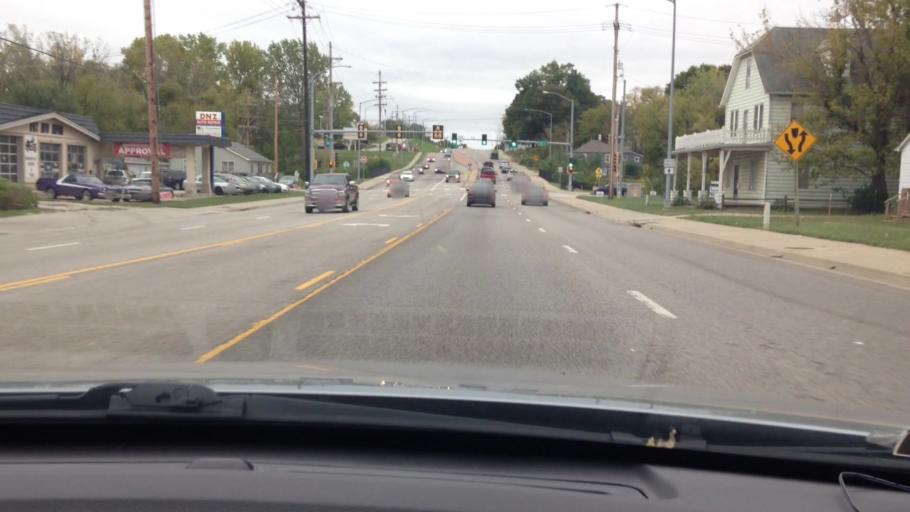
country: US
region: Kansas
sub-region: Leavenworth County
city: Lansing
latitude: 39.2527
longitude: -94.9001
